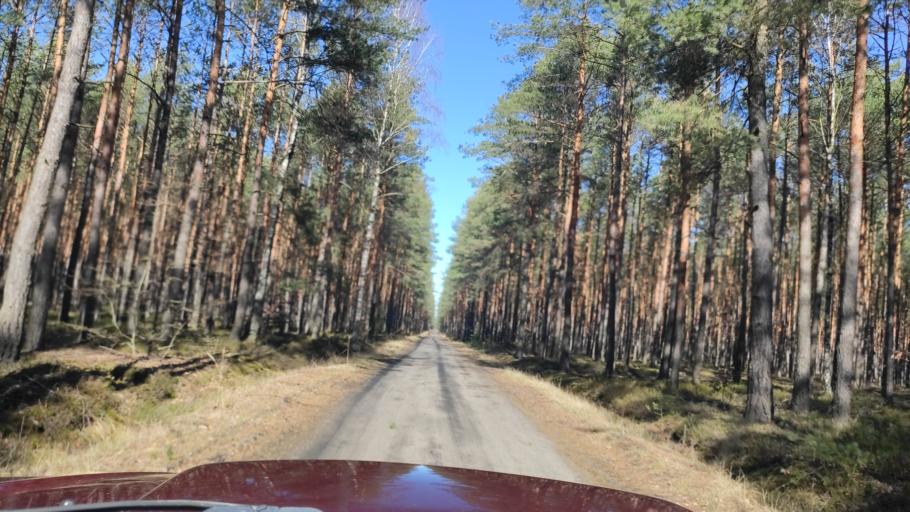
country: PL
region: Masovian Voivodeship
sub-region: Powiat zwolenski
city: Zwolen
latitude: 51.4176
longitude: 21.5538
